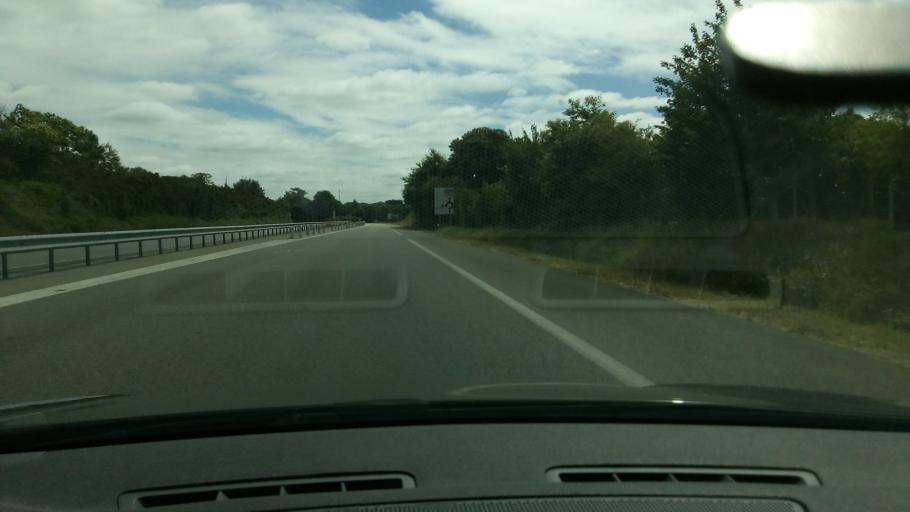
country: FR
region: Brittany
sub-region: Departement du Finistere
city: Ergue-Gaberic
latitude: 47.9782
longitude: -4.0202
